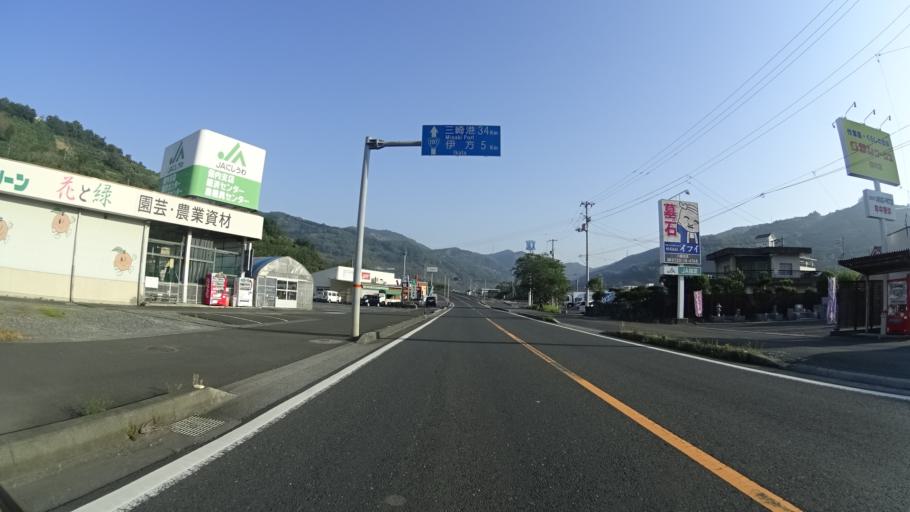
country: JP
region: Ehime
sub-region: Nishiuwa-gun
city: Ikata-cho
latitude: 33.4863
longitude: 132.3986
